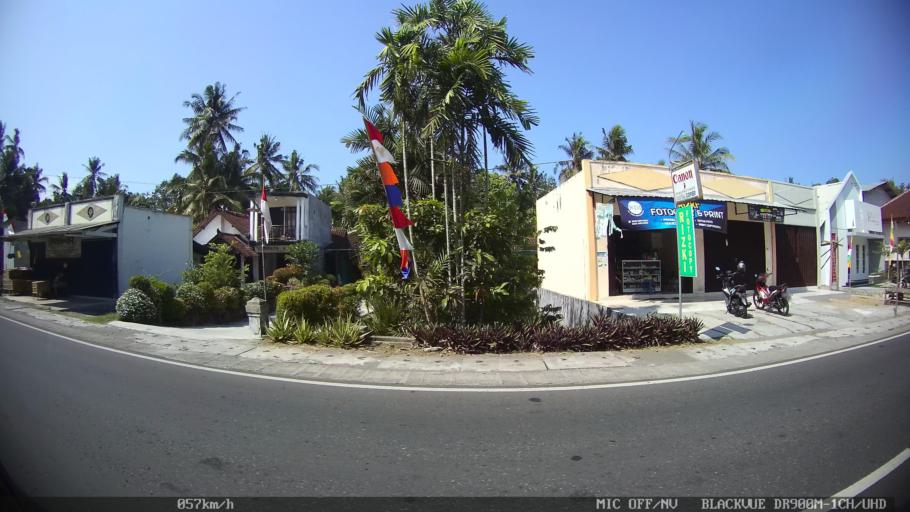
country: ID
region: Daerah Istimewa Yogyakarta
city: Srandakan
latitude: -7.9299
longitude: 110.2052
